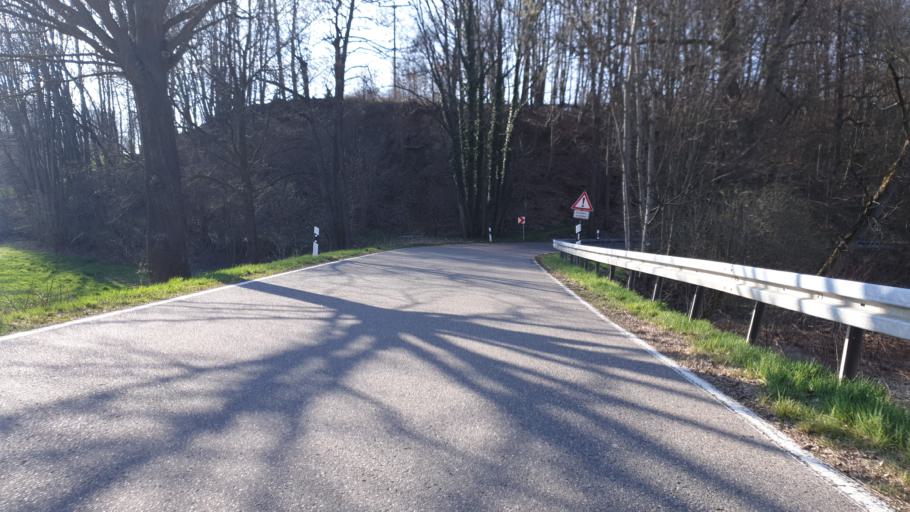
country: DE
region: Saxony
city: Taura
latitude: 50.9377
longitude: 12.8394
